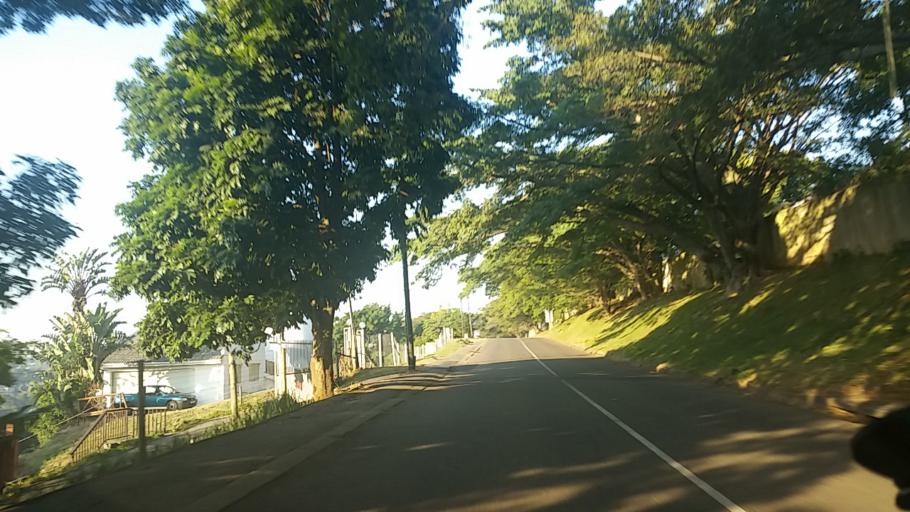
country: ZA
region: KwaZulu-Natal
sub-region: eThekwini Metropolitan Municipality
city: Berea
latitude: -29.8534
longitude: 30.9129
